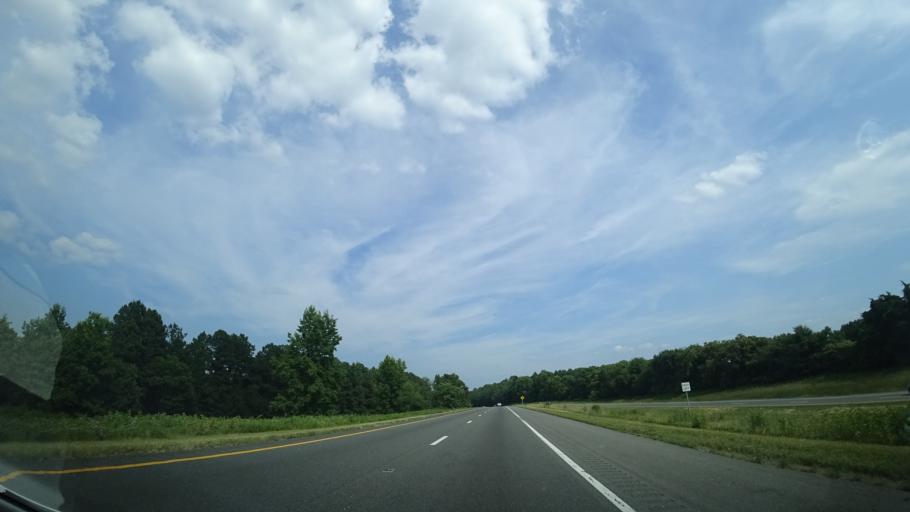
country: US
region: Virginia
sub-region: Henrico County
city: Chamberlayne
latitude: 37.6559
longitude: -77.4452
